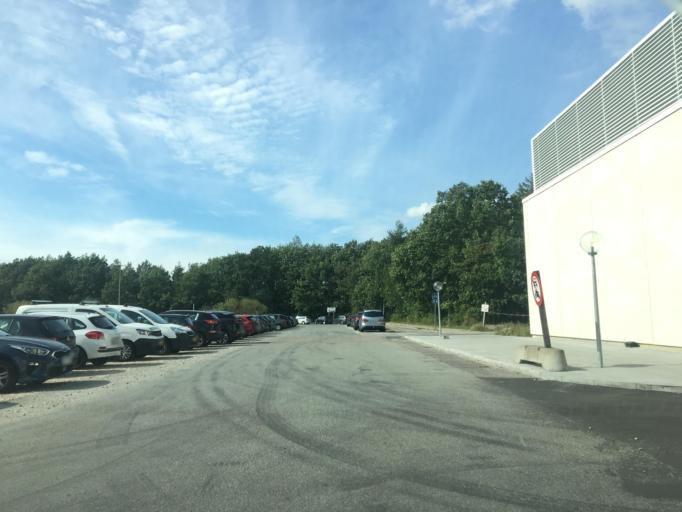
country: DK
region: Capital Region
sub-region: Herlev Kommune
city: Herlev
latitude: 55.7334
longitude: 12.4401
